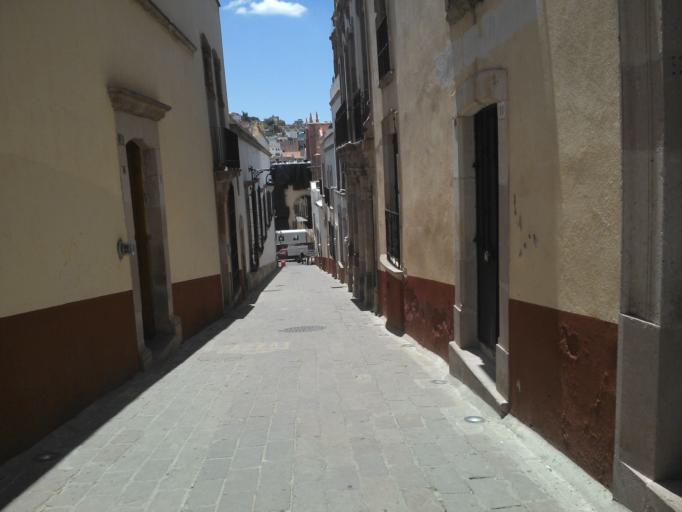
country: MX
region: Zacatecas
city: Zacatecas
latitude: 22.7763
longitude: -102.5730
